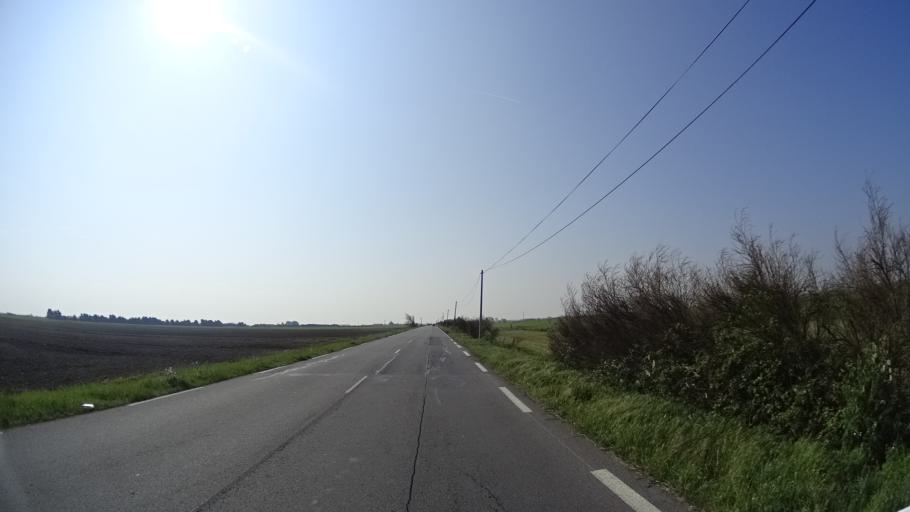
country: FR
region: Pays de la Loire
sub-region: Departement de la Loire-Atlantique
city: Bourgneuf-en-Retz
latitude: 47.0228
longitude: -1.9608
